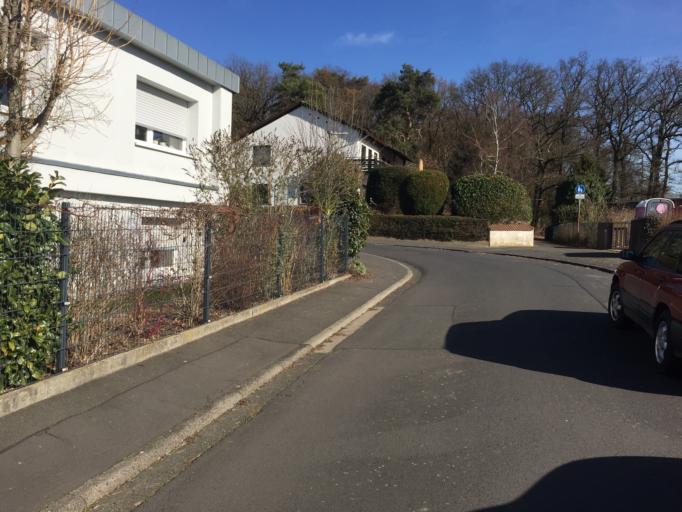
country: DE
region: Hesse
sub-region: Regierungsbezirk Giessen
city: Langgons
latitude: 50.5368
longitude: 8.6880
